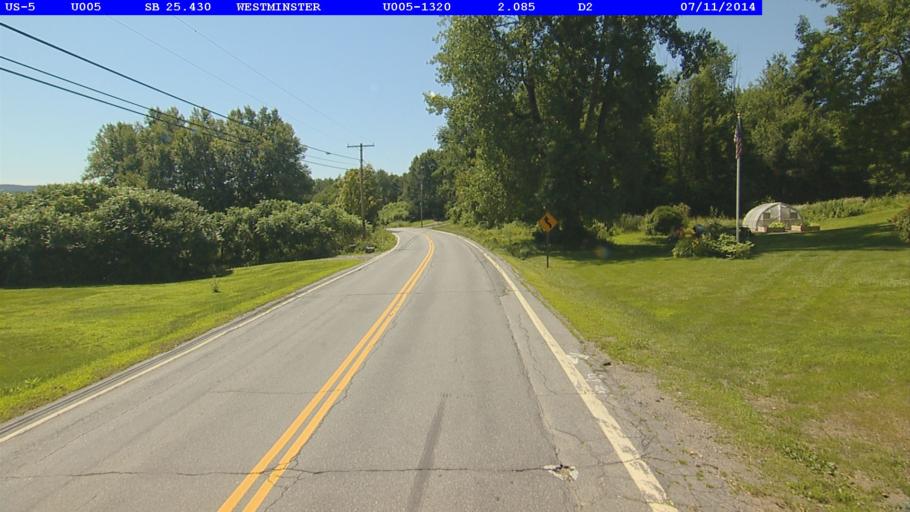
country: US
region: Vermont
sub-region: Windham County
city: Bellows Falls
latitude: 43.0489
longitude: -72.4693
